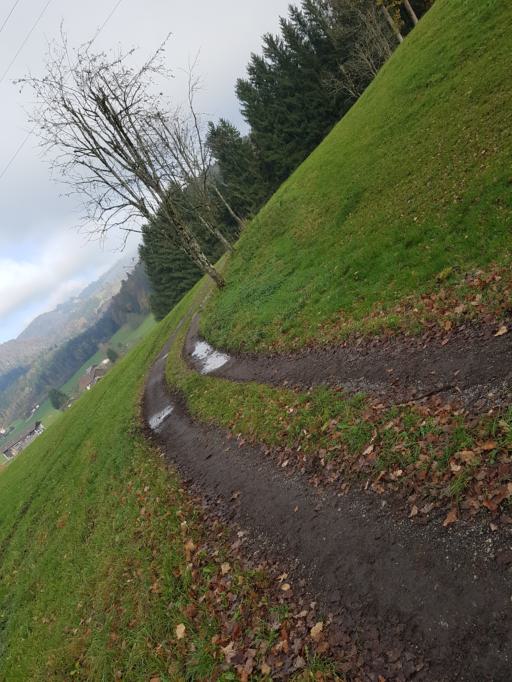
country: AT
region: Salzburg
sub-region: Politischer Bezirk Hallein
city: Adnet
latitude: 47.6752
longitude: 13.1447
